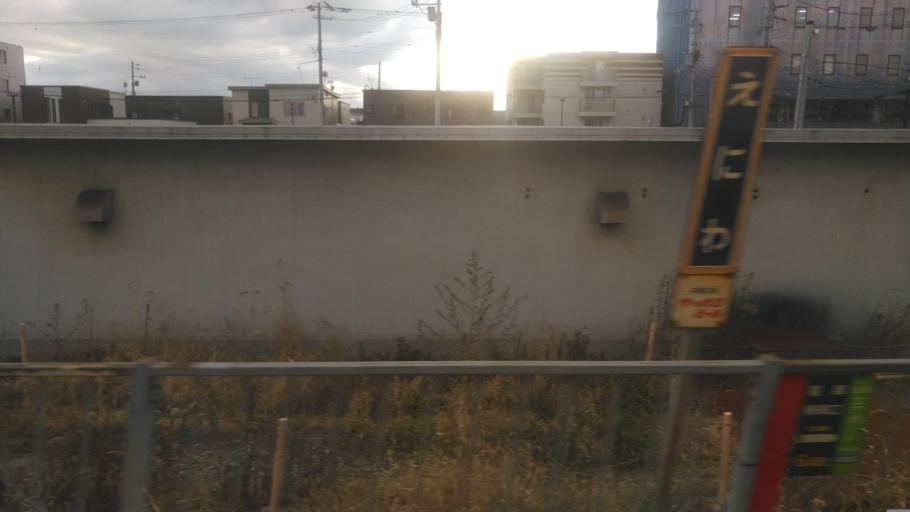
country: JP
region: Hokkaido
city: Chitose
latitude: 42.8823
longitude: 141.5872
